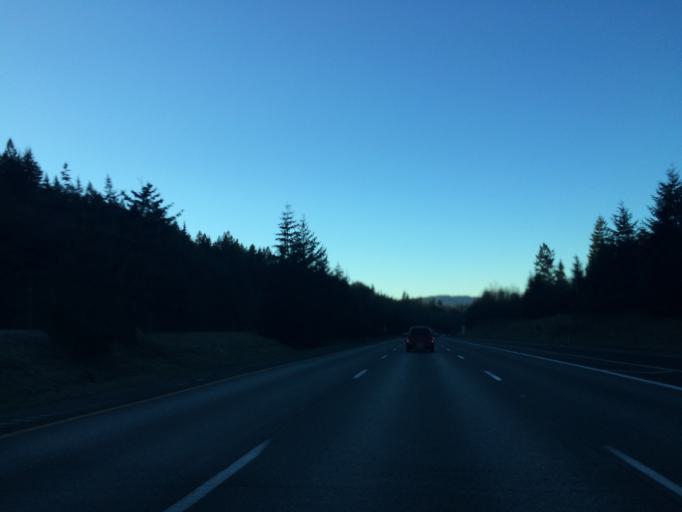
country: US
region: Washington
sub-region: King County
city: Issaquah
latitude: 47.5312
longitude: -121.9849
